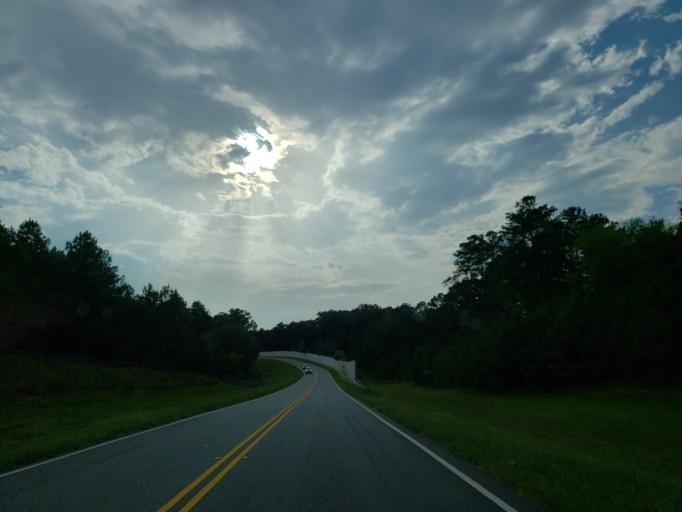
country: US
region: Georgia
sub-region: Bartow County
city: Euharlee
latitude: 34.1368
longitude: -84.9307
